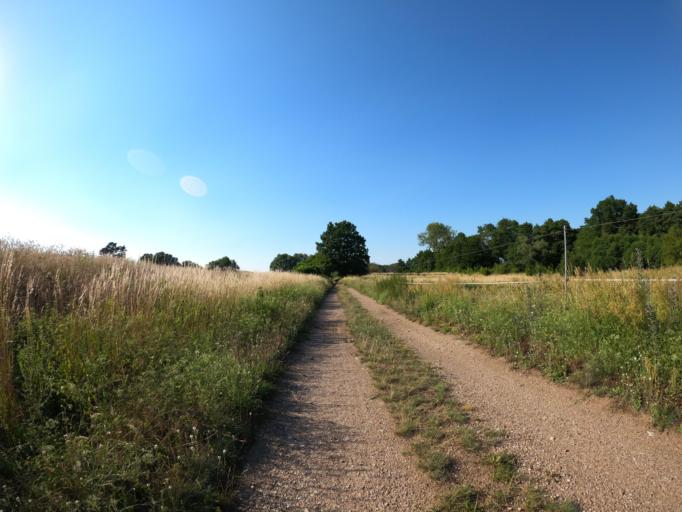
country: DE
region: Brandenburg
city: Gartz
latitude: 53.2297
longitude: 14.3682
